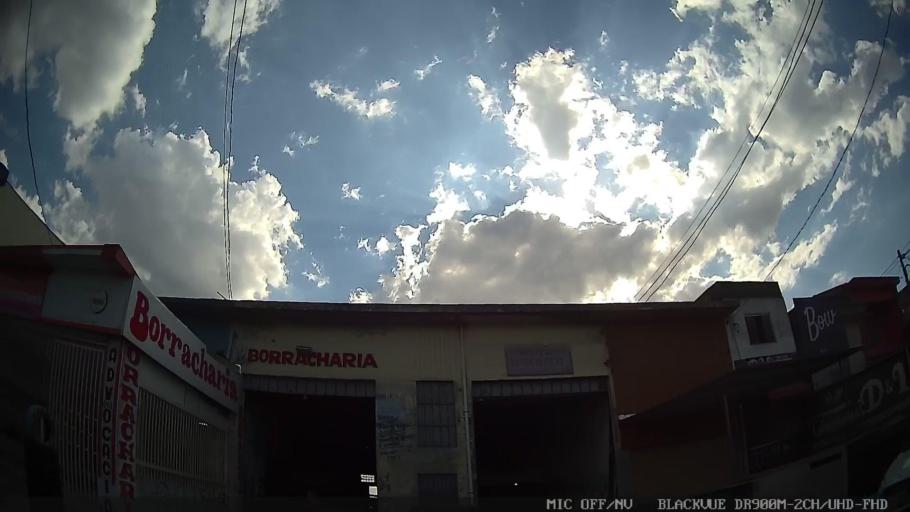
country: BR
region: Sao Paulo
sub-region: Ferraz De Vasconcelos
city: Ferraz de Vasconcelos
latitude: -23.5220
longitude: -46.4185
